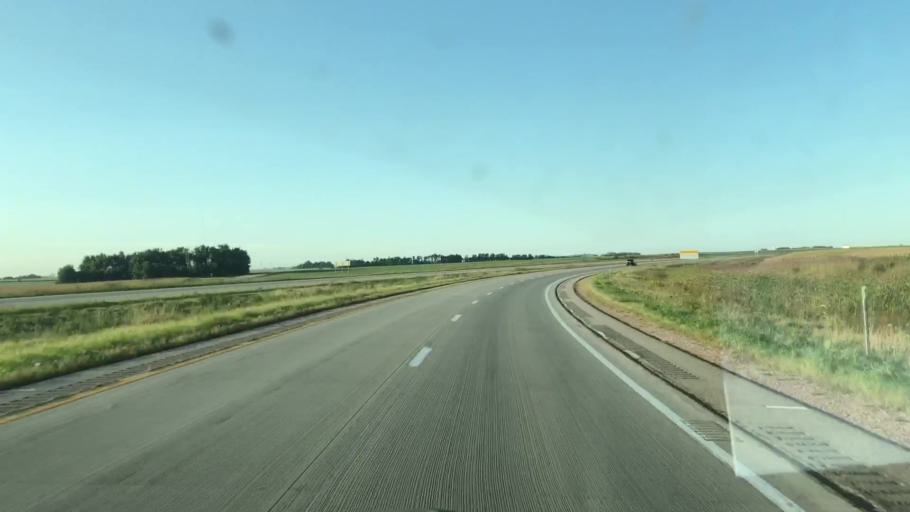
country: US
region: Iowa
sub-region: Osceola County
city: Sibley
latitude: 43.4979
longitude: -95.6836
